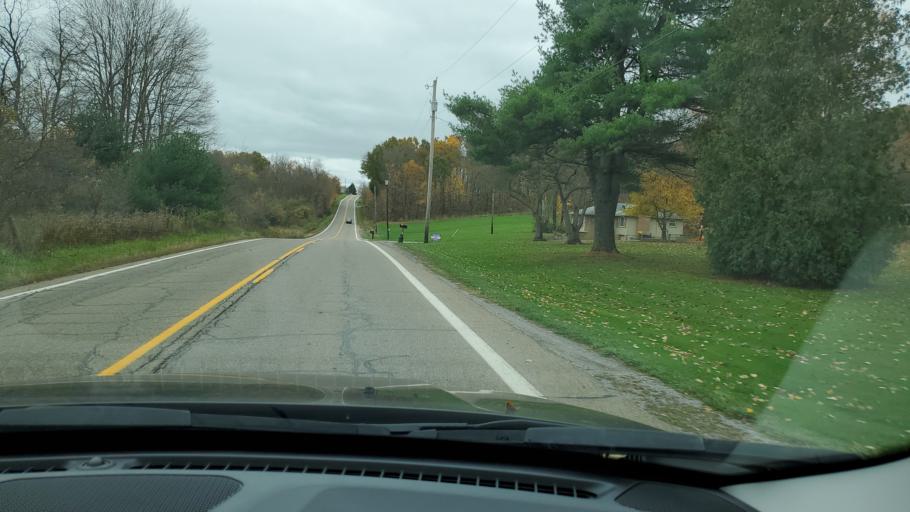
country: US
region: Ohio
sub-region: Columbiana County
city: New Waterford
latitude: 40.9030
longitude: -80.5864
